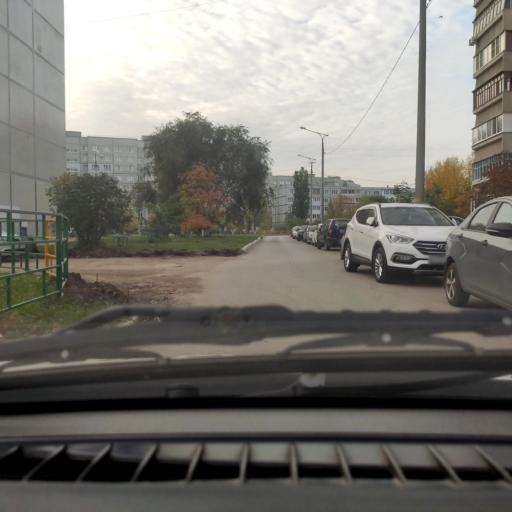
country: RU
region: Samara
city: Tol'yatti
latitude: 53.5406
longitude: 49.3987
